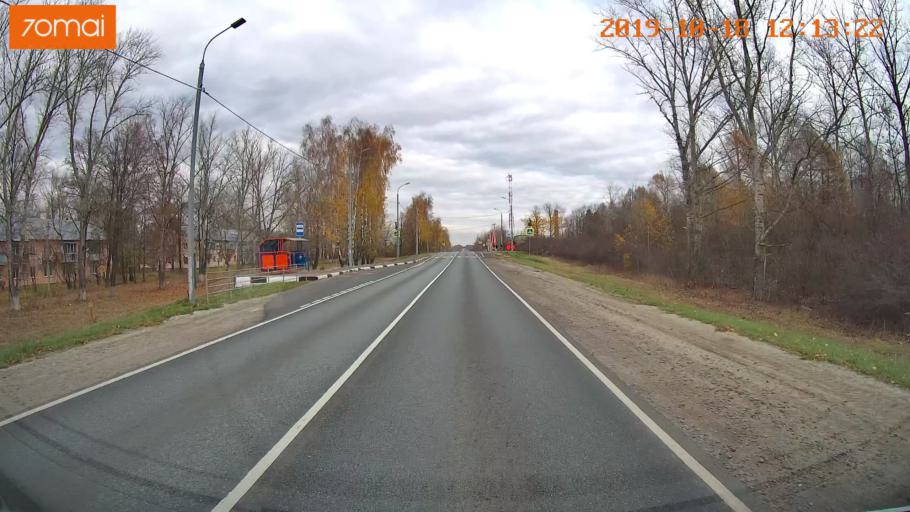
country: RU
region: Rjazan
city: Zakharovo
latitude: 54.4204
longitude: 39.3693
